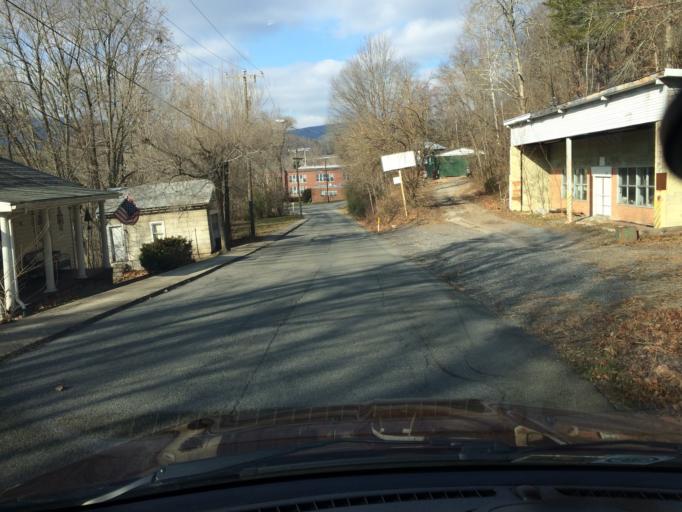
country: US
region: Virginia
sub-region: Alleghany County
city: Clifton Forge
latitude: 37.8205
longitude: -79.8233
